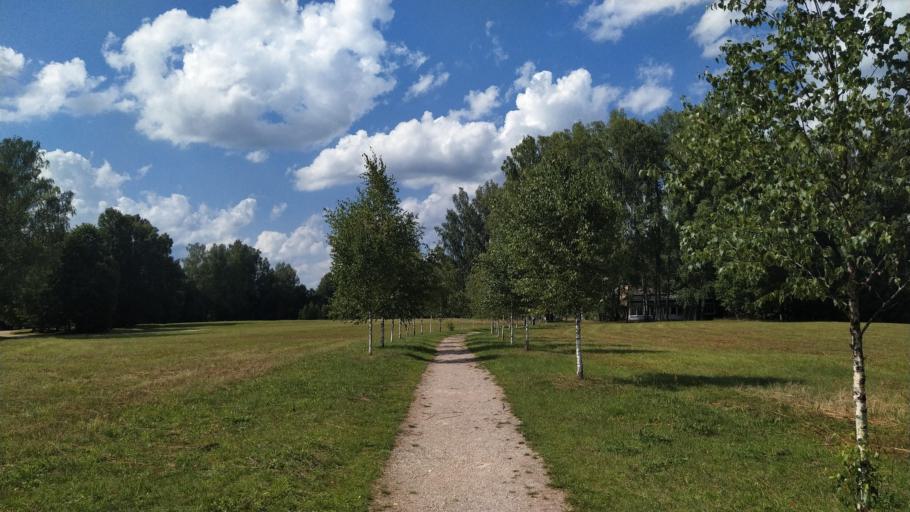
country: RU
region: Pskov
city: Pushkinskiye Gory
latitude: 57.0600
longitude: 28.9270
